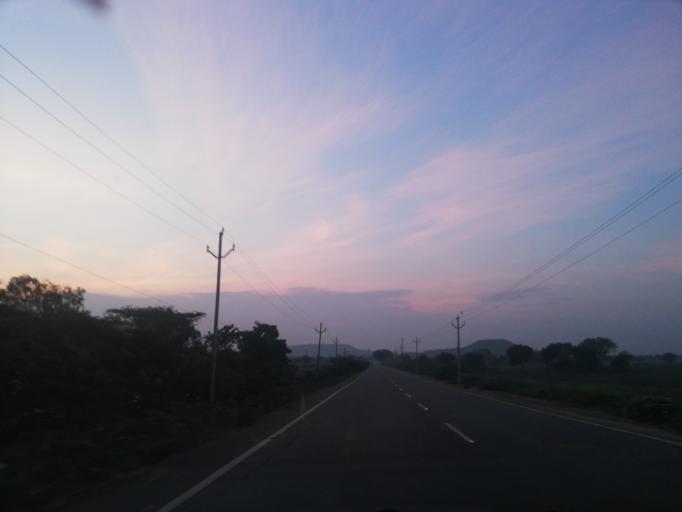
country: IN
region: Andhra Pradesh
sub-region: Guntur
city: Macherla
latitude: 16.6820
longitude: 79.2590
